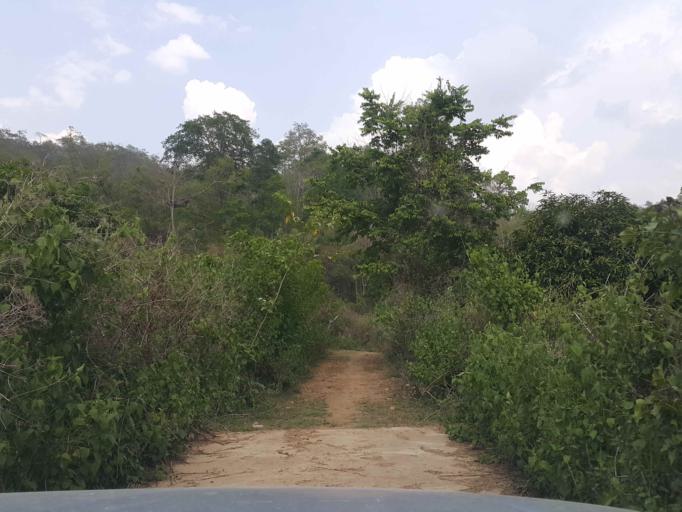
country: TH
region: Chiang Mai
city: Wiang Haeng
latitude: 19.3978
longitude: 98.7235
